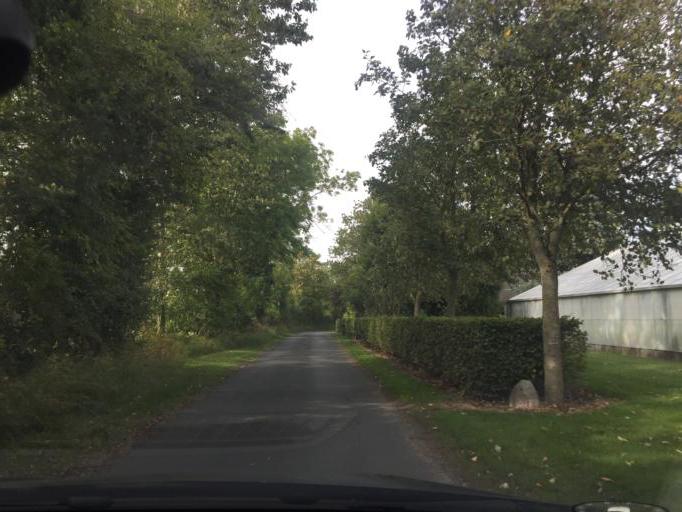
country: DK
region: South Denmark
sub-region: Faaborg-Midtfyn Kommune
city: Arslev
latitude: 55.3456
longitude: 10.5131
